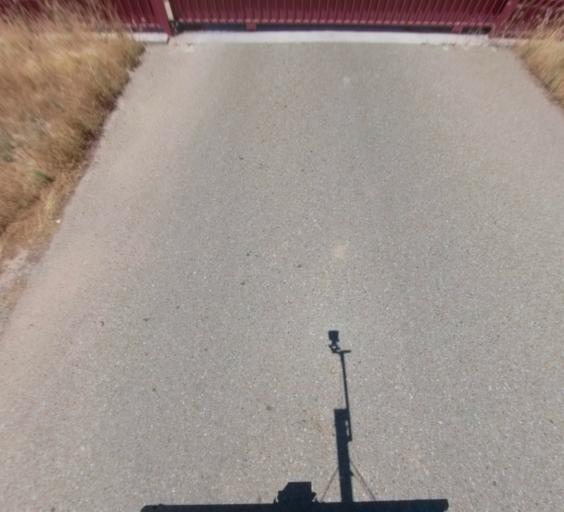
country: US
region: California
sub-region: Madera County
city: Bonadelle Ranchos-Madera Ranchos
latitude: 36.9328
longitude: -119.8317
